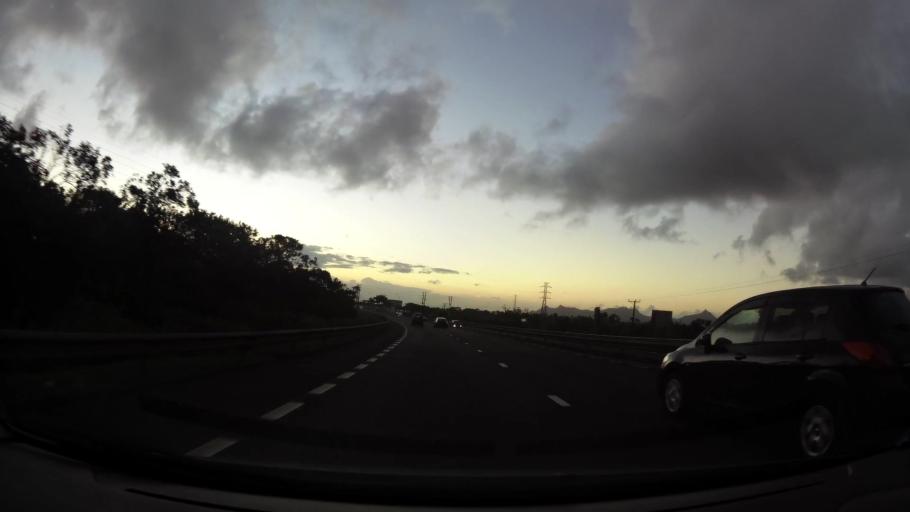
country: MU
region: Plaines Wilhems
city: Curepipe
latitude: -20.2972
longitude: 57.5349
